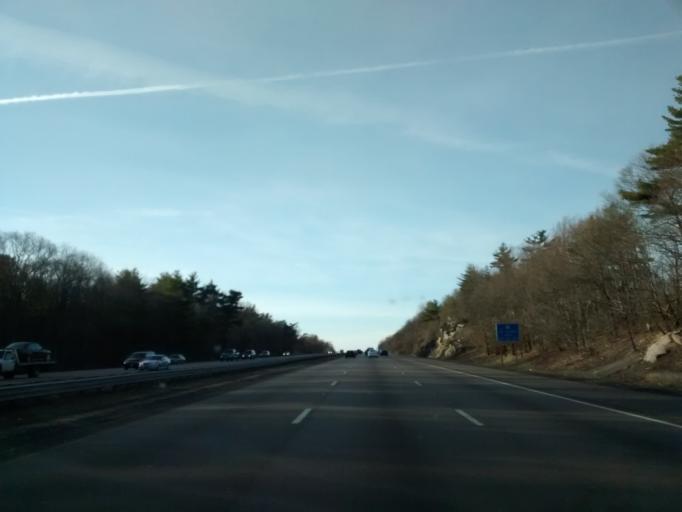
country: US
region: Massachusetts
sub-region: Norfolk County
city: Randolph
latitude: 42.1688
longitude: -71.0722
